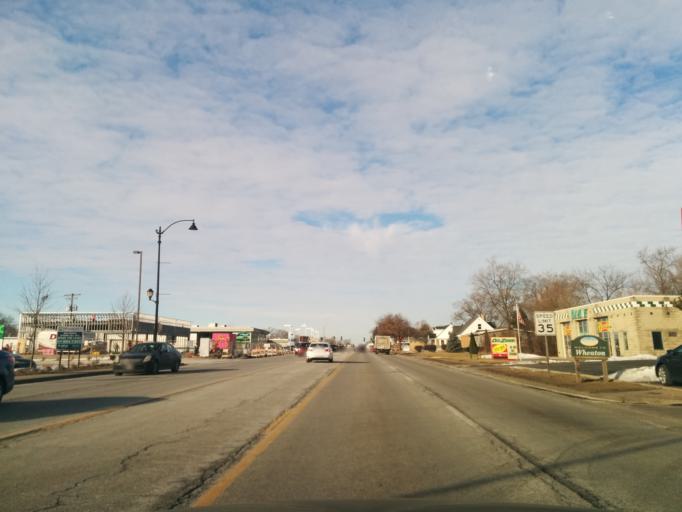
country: US
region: Illinois
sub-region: DuPage County
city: Glen Ellyn
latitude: 41.8592
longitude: -88.0789
